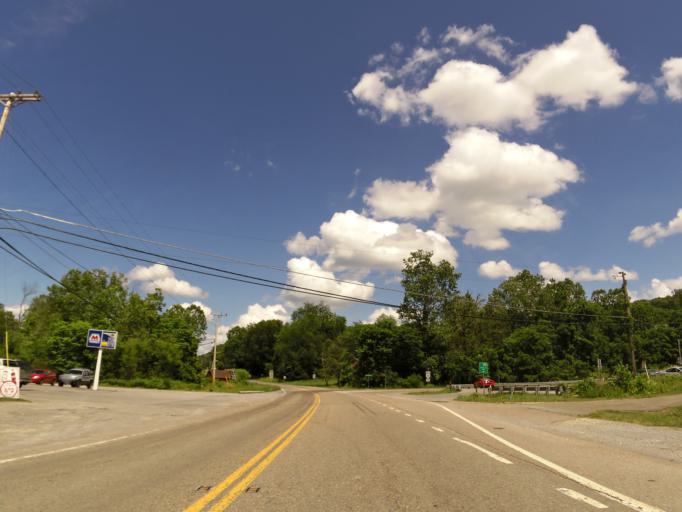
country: US
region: Virginia
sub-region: Lee County
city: Jonesville
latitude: 36.6874
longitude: -83.1024
